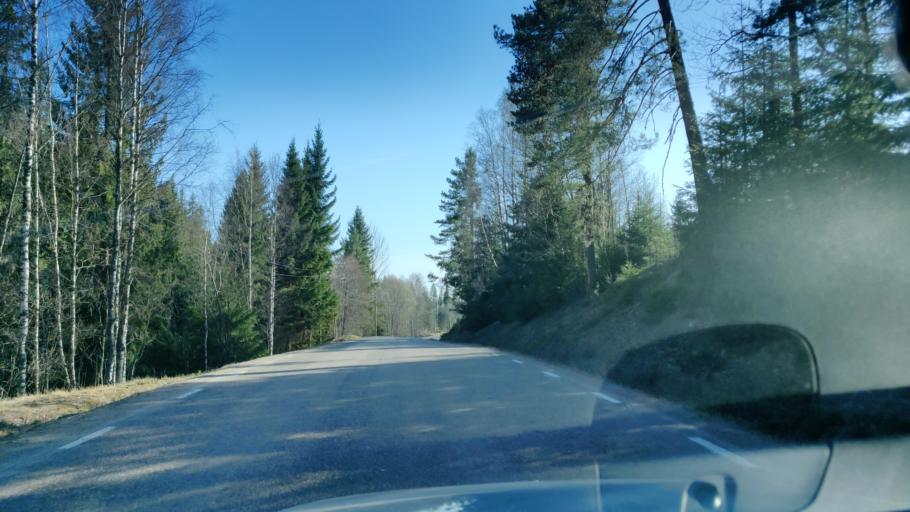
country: SE
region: Vaermland
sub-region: Sunne Kommun
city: Sunne
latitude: 59.9887
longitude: 13.2705
